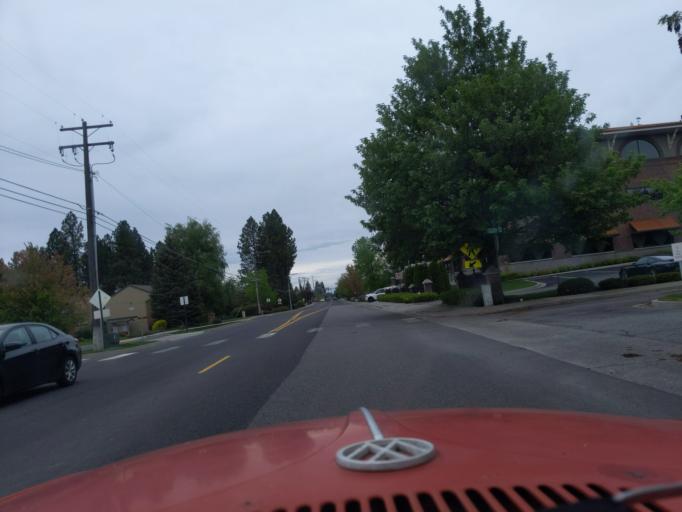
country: US
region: Washington
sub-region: Spokane County
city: Spokane
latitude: 47.5994
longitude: -117.3685
